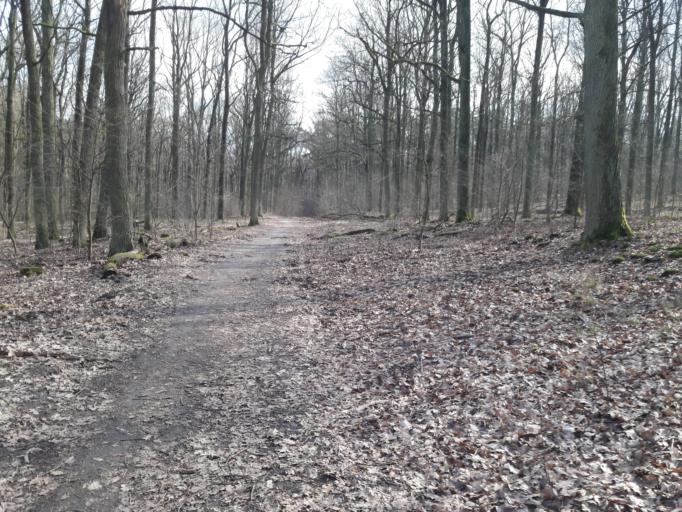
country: PL
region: Greater Poland Voivodeship
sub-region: Powiat poznanski
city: Suchy Las
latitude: 52.4812
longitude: 16.8956
